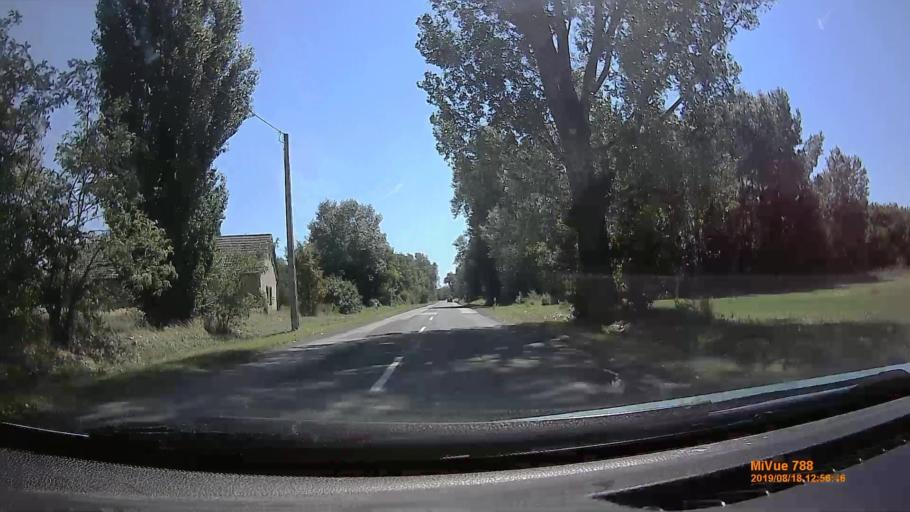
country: HU
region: Fejer
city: Sarkeresztur
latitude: 47.0211
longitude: 18.5432
